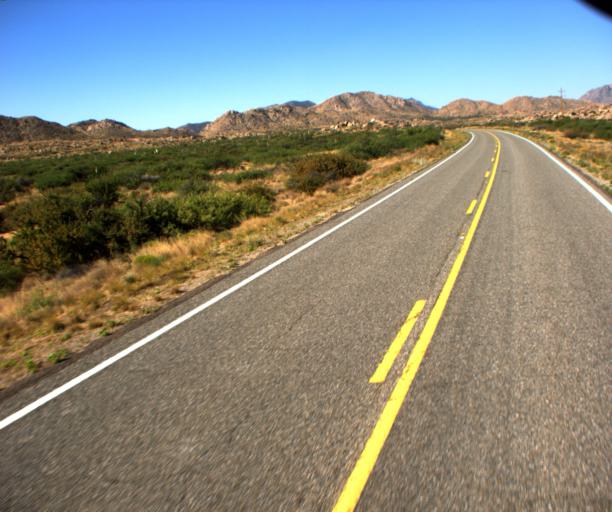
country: US
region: Arizona
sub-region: Graham County
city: Swift Trail Junction
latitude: 32.5766
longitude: -109.7129
